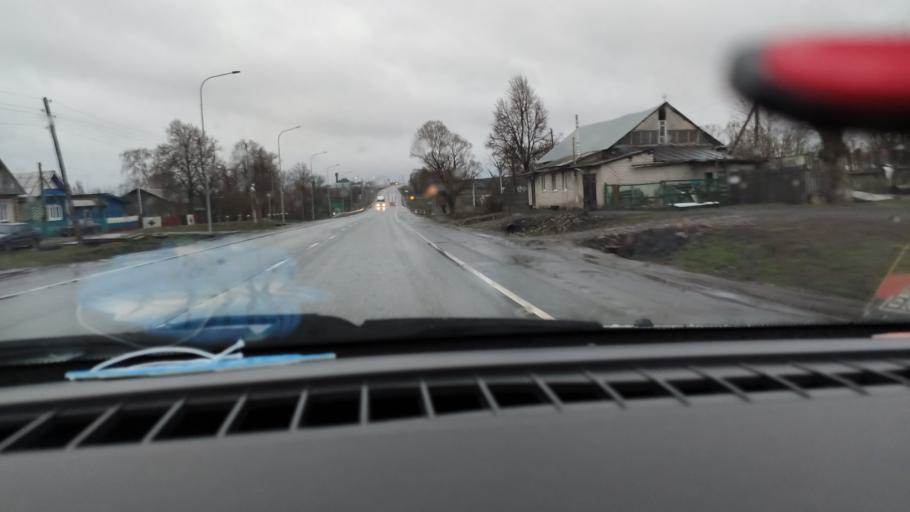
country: RU
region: Tatarstan
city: Mendeleyevsk
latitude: 56.0307
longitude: 52.3759
